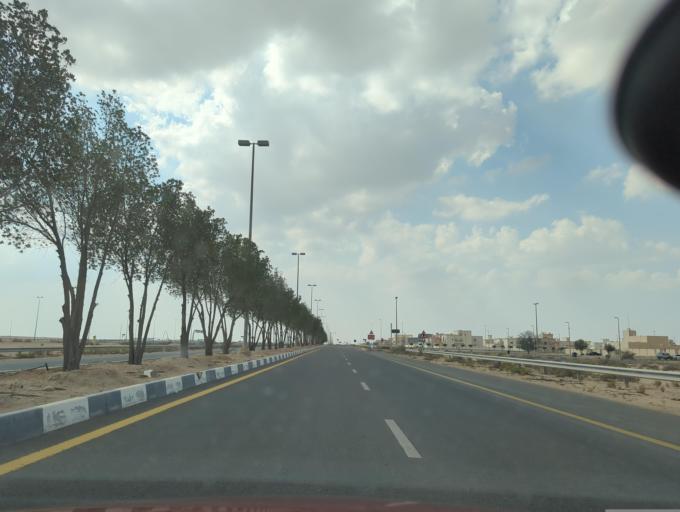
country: AE
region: Abu Dhabi
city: Abu Dhabi
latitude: 24.3634
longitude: 54.7189
